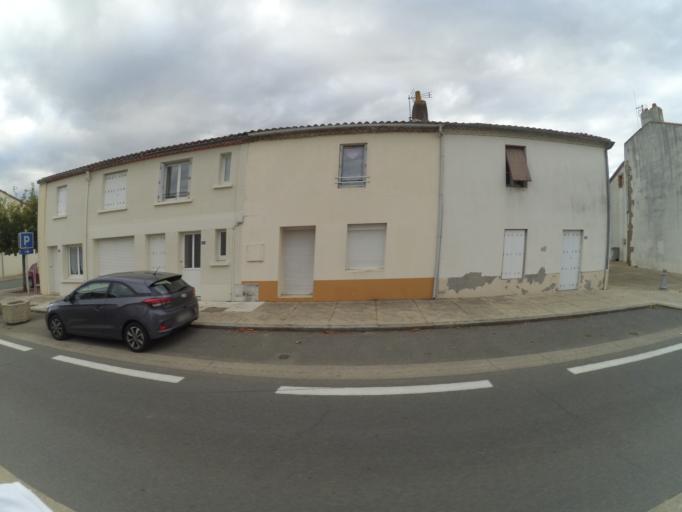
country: FR
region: Pays de la Loire
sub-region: Departement de la Vendee
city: Saint-Andre-Treize-Voies
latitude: 46.9071
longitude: -1.3776
